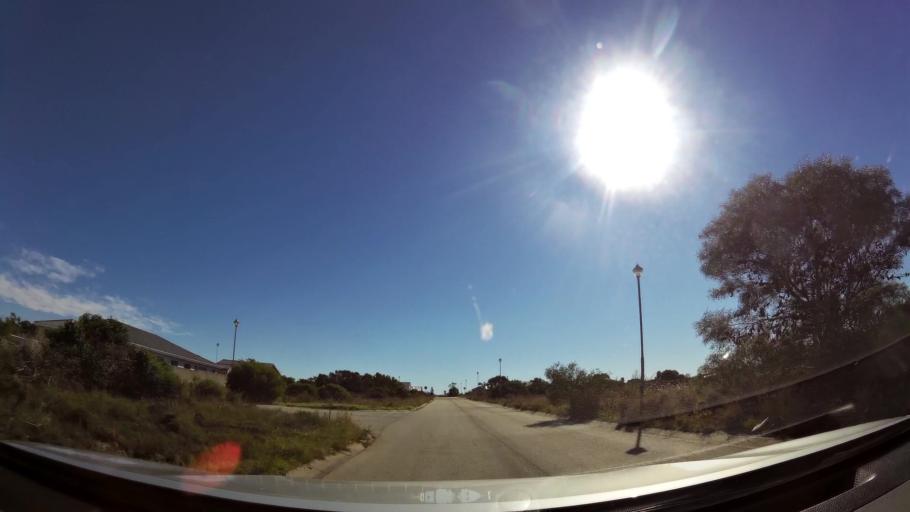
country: ZA
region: Eastern Cape
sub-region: Cacadu District Municipality
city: Jeffrey's Bay
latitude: -34.0352
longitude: 24.9083
